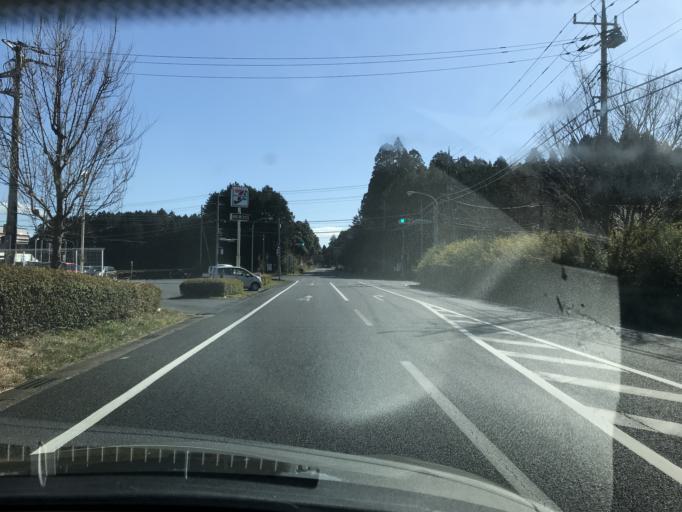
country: JP
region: Chiba
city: Sawara
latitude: 35.8175
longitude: 140.5196
